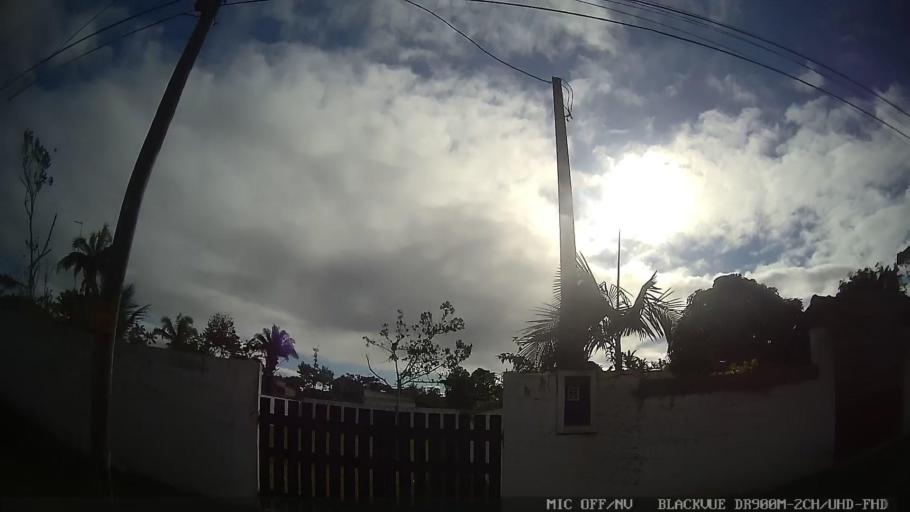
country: BR
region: Sao Paulo
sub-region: Peruibe
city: Peruibe
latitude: -24.2361
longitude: -46.9115
